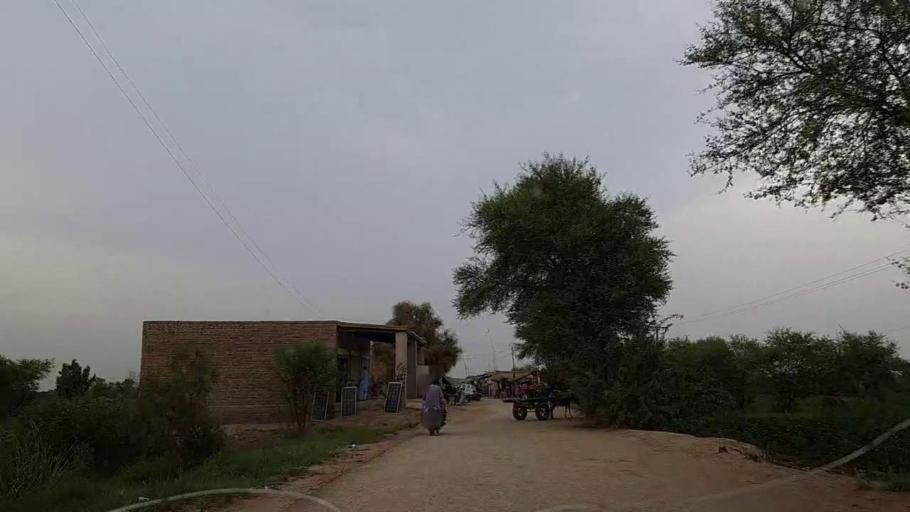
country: PK
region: Sindh
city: Mirpur Mathelo
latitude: 27.8462
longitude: 69.6270
